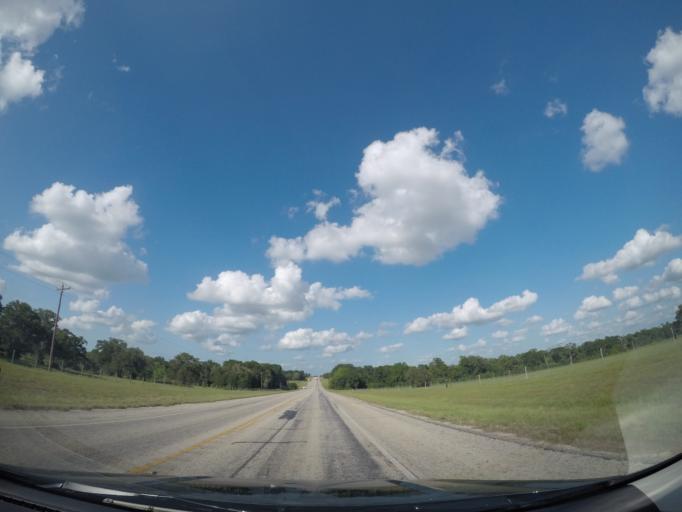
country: US
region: Texas
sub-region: Lavaca County
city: Hallettsville
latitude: 29.4551
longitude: -96.8493
